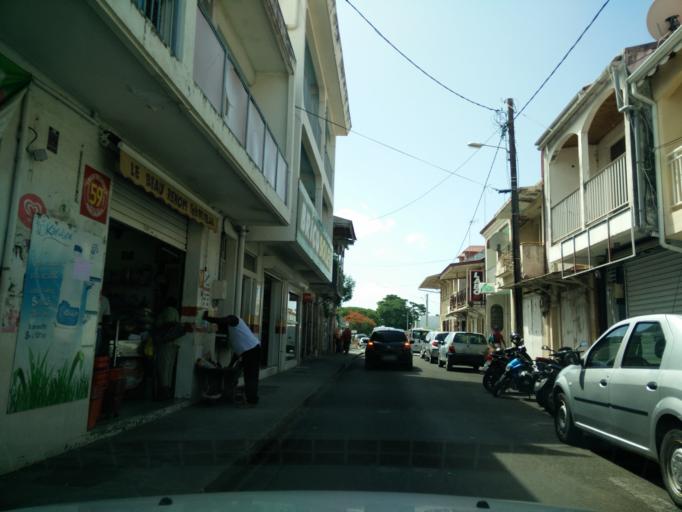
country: GP
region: Guadeloupe
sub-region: Guadeloupe
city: Grand-Bourg
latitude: 15.8823
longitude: -61.3149
